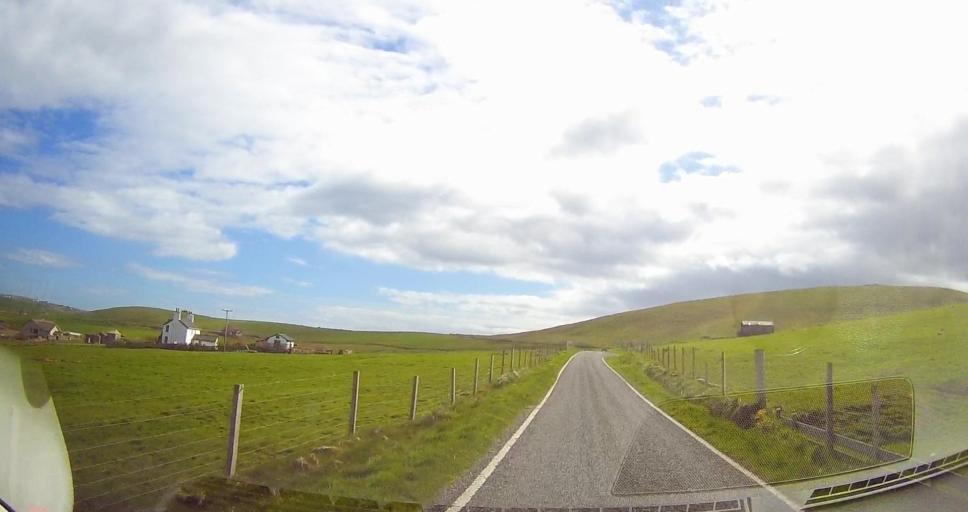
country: GB
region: Scotland
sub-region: Shetland Islands
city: Sandwick
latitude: 59.9301
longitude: -1.3449
